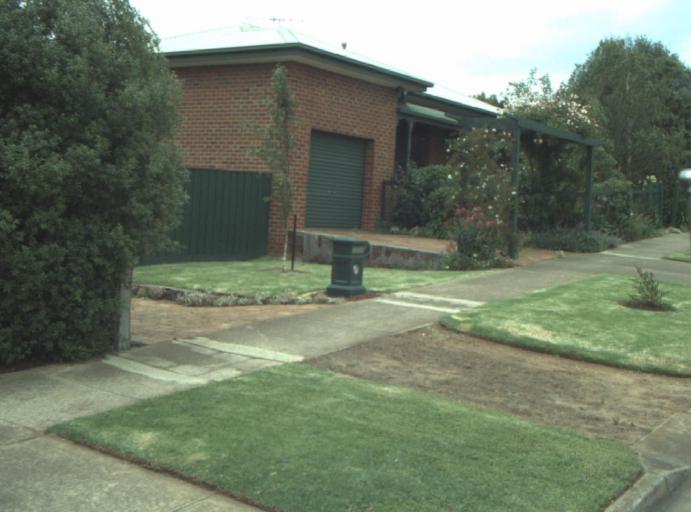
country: AU
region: Victoria
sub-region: Greater Geelong
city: Wandana Heights
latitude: -38.2081
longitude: 144.3025
